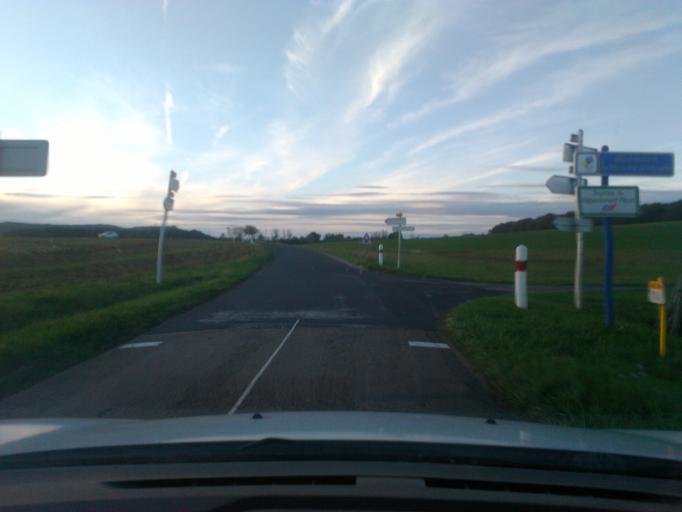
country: FR
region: Lorraine
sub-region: Departement de Meurthe-et-Moselle
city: Vezelise
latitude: 48.4074
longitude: 6.1485
